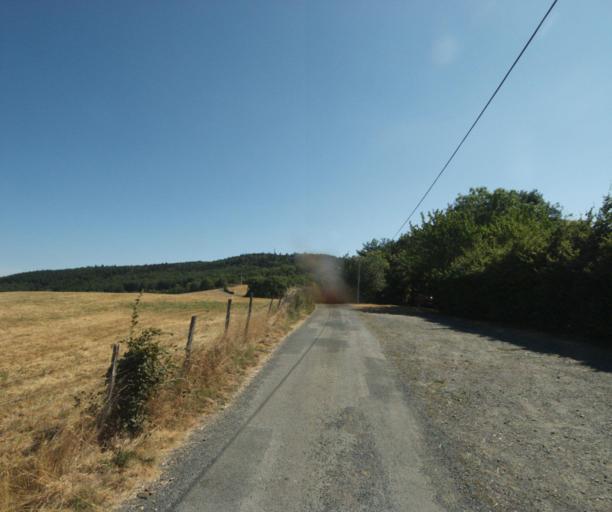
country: FR
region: Rhone-Alpes
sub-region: Departement du Rhone
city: Saint-Romain-de-Popey
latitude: 45.8161
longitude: 4.5079
